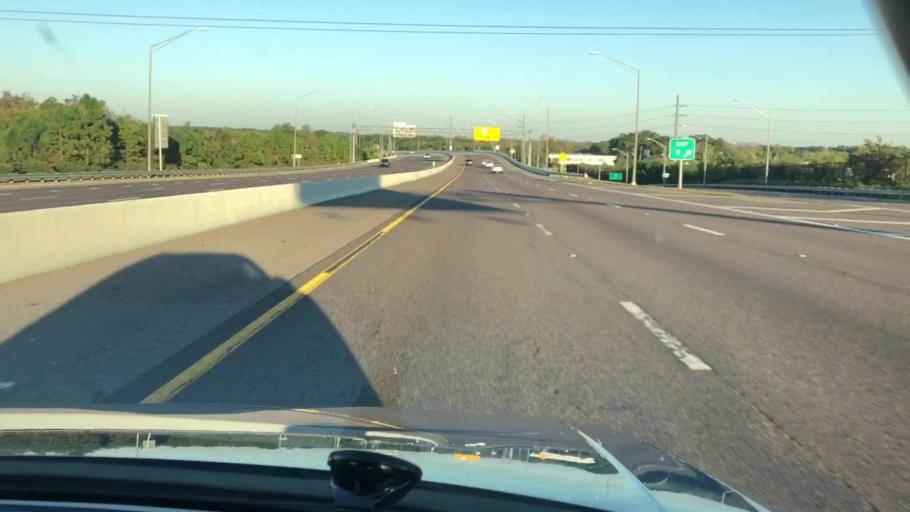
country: US
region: Florida
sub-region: Orange County
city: Lockhart
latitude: 28.6334
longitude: -81.4561
